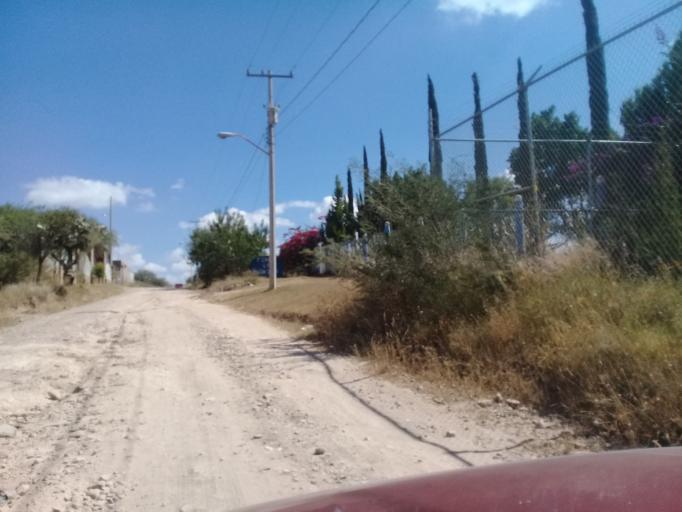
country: MX
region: Aguascalientes
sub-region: Aguascalientes
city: San Sebastian [Fraccionamiento]
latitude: 21.7792
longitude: -102.2578
